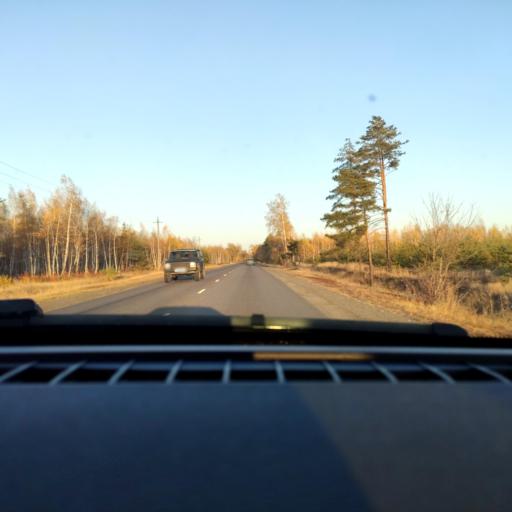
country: RU
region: Voronezj
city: Maslovka
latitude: 51.5794
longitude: 39.2716
